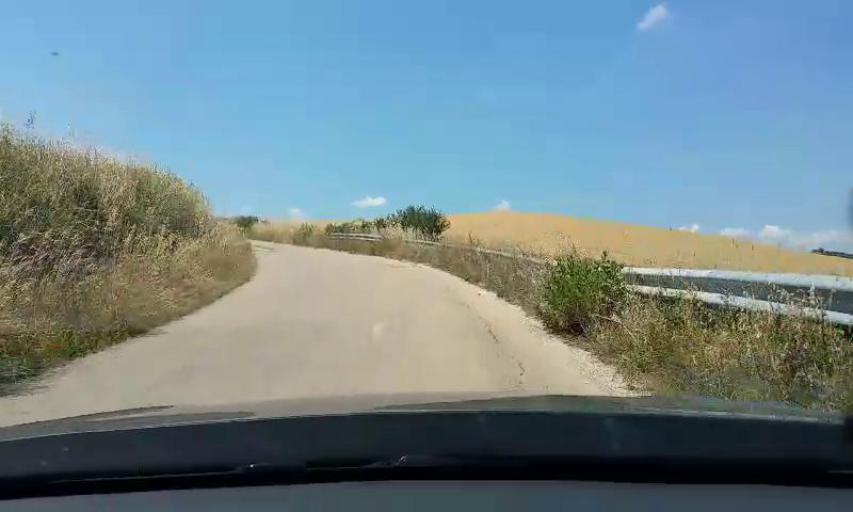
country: IT
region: Molise
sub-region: Provincia di Campobasso
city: Montecilfone
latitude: 41.9220
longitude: 14.8455
